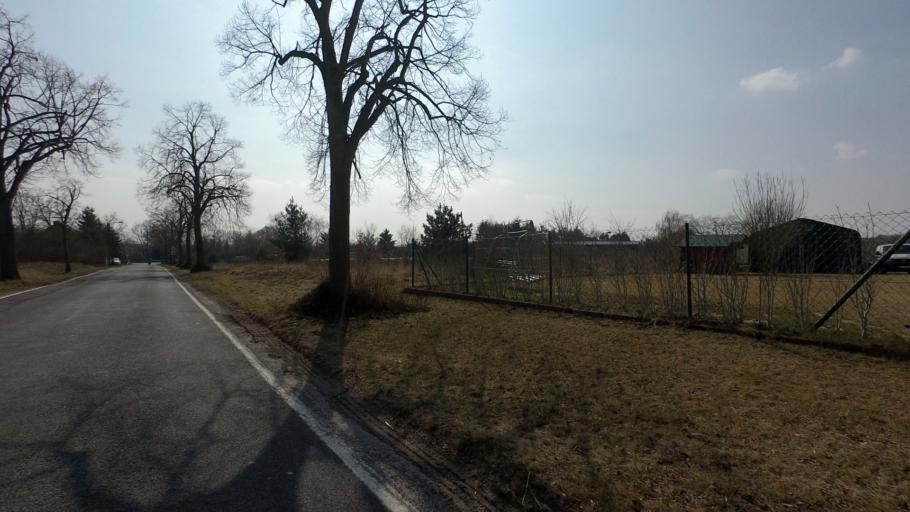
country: DE
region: Brandenburg
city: Gross Kreutz
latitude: 52.4204
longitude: 12.7917
